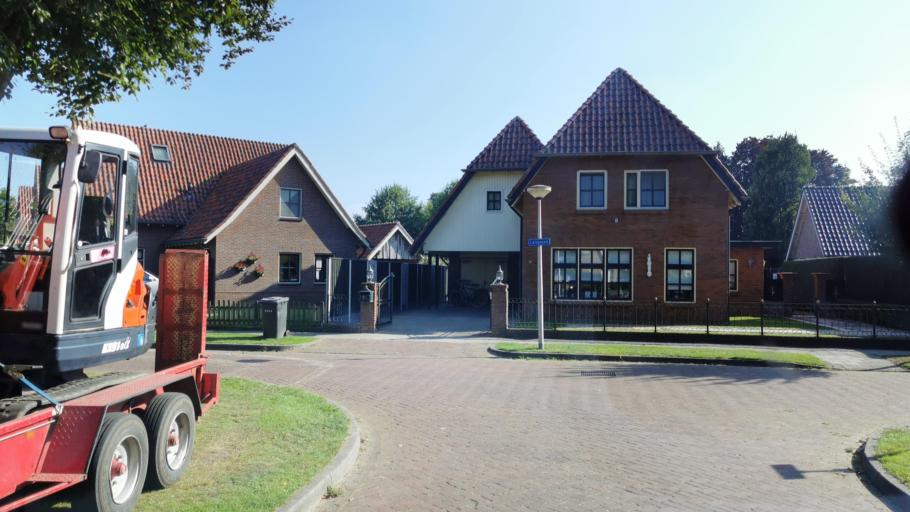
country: DE
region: Lower Saxony
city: Lage
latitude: 52.4064
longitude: 6.9509
